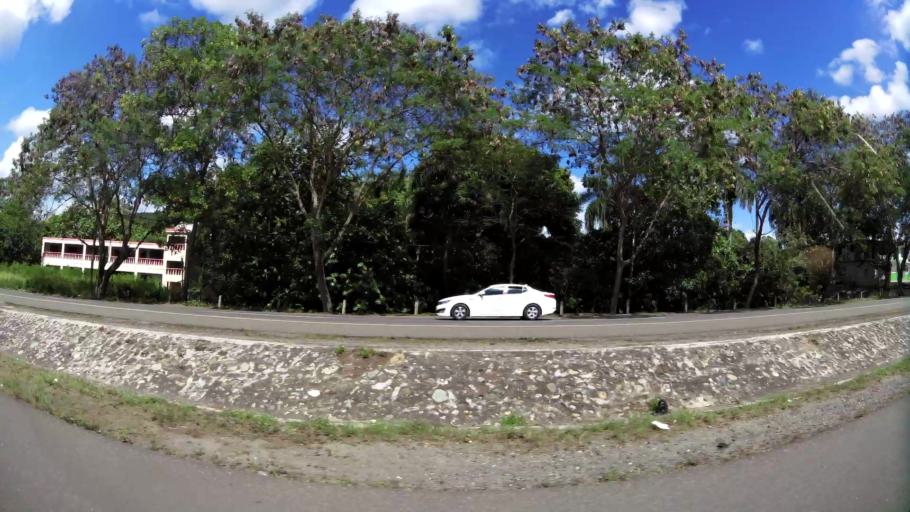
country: DO
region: La Vega
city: Rio Verde Arriba
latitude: 19.2898
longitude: -70.5754
